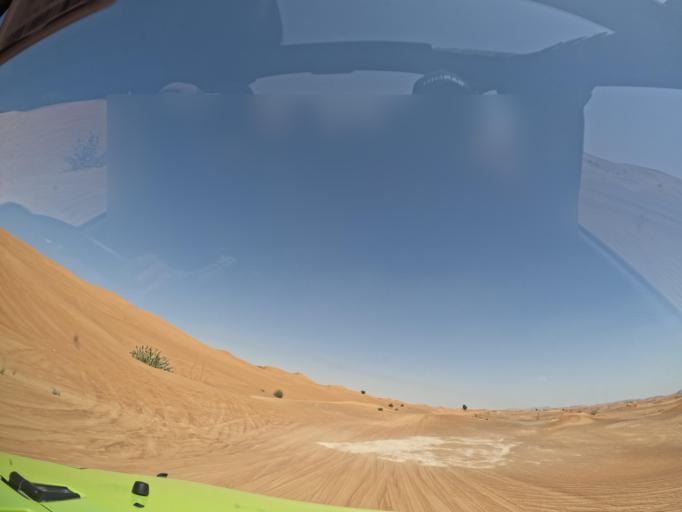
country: AE
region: Ash Shariqah
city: Adh Dhayd
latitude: 24.9976
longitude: 55.7262
